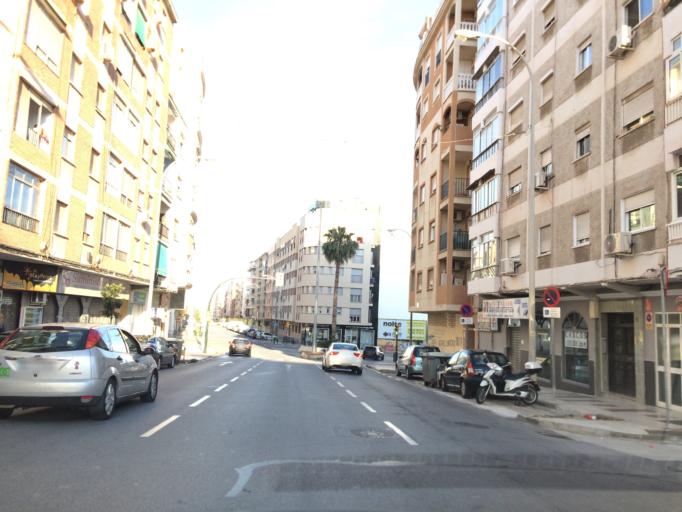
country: ES
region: Andalusia
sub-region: Provincia de Malaga
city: Malaga
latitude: 36.7268
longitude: -4.4396
